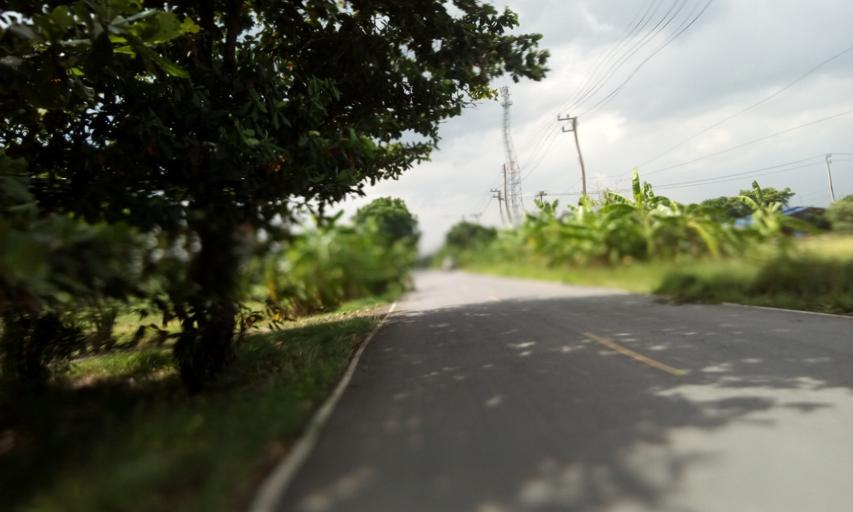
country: TH
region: Pathum Thani
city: Ban Rangsit
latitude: 14.0390
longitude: 100.8476
